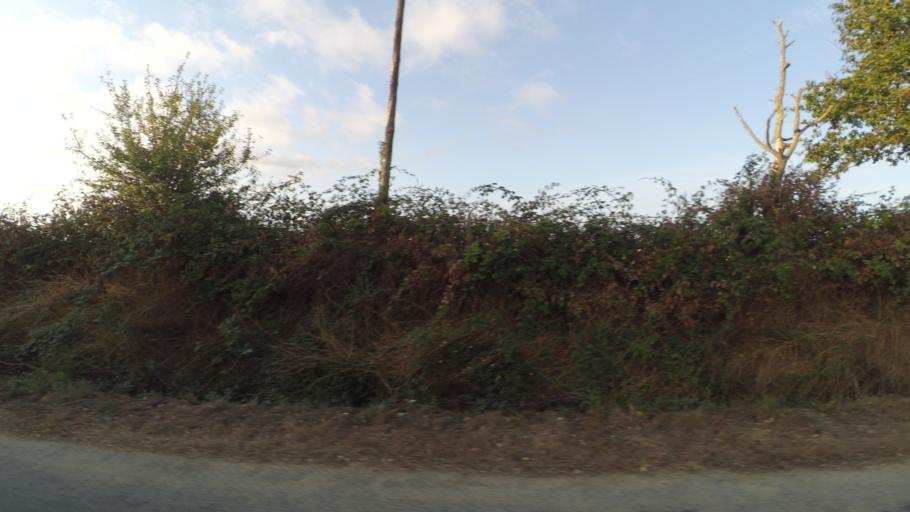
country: FR
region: Pays de la Loire
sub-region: Departement de la Loire-Atlantique
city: Vieillevigne
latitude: 46.9799
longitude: -1.4490
